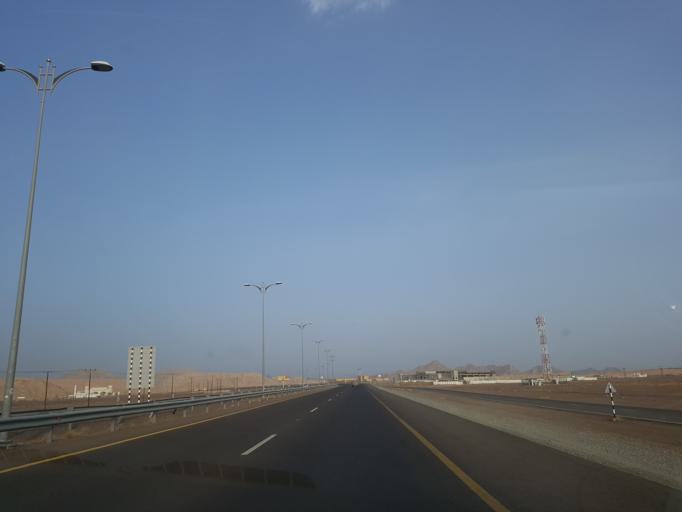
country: OM
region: Al Buraimi
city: Al Buraymi
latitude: 24.2329
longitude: 55.9225
